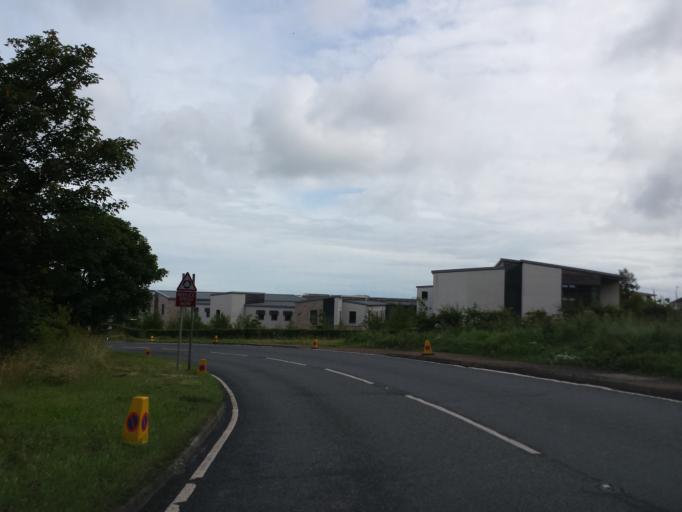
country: GB
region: Scotland
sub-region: Fife
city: Saint Andrews
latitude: 56.3269
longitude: -2.8075
